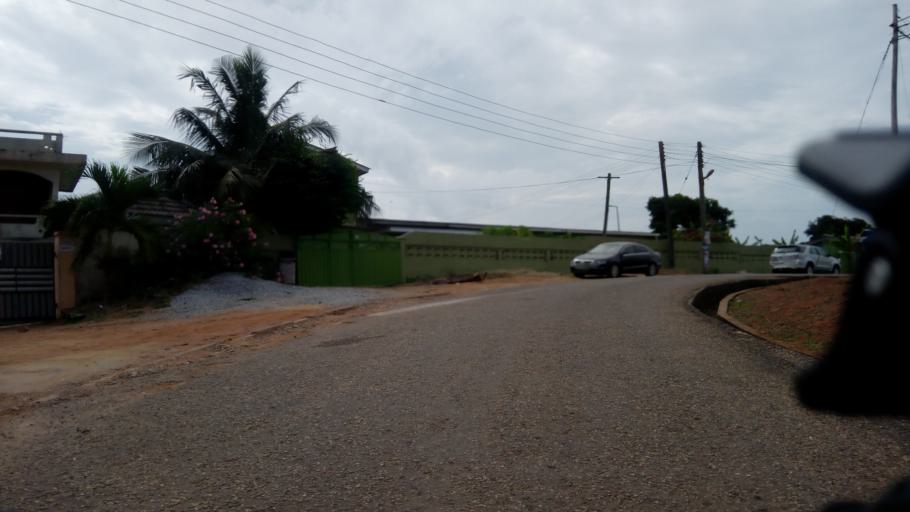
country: GH
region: Central
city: Cape Coast
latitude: 5.1063
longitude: -1.2760
